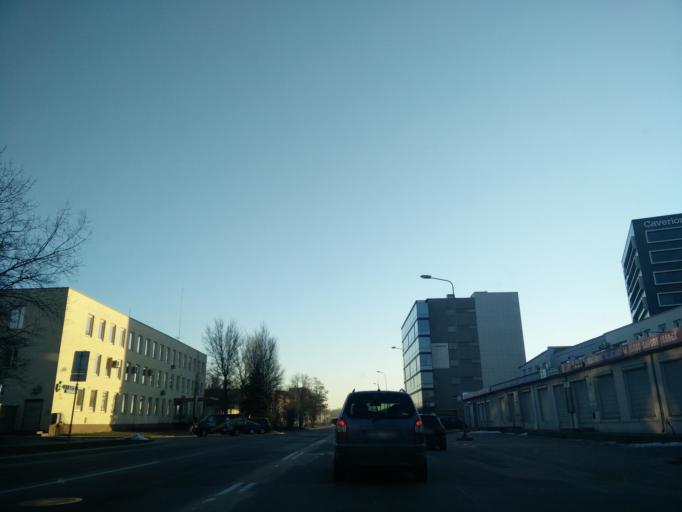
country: LT
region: Vilnius County
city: Vilkpede
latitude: 54.6672
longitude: 25.2538
